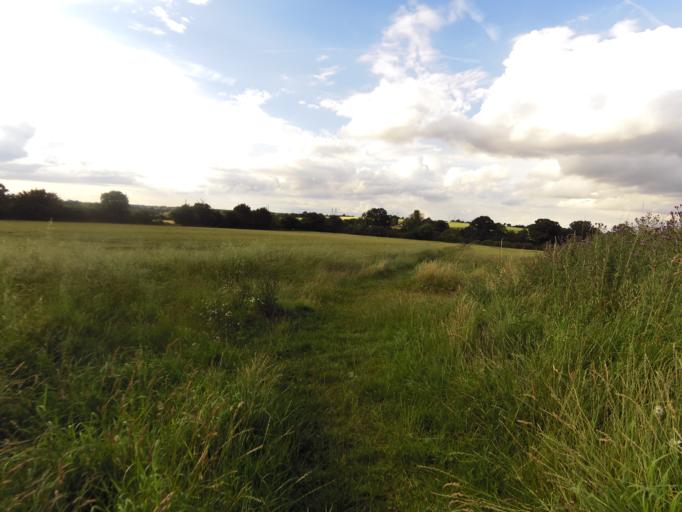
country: GB
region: England
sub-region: Suffolk
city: Ipswich
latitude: 52.0824
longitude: 1.1635
